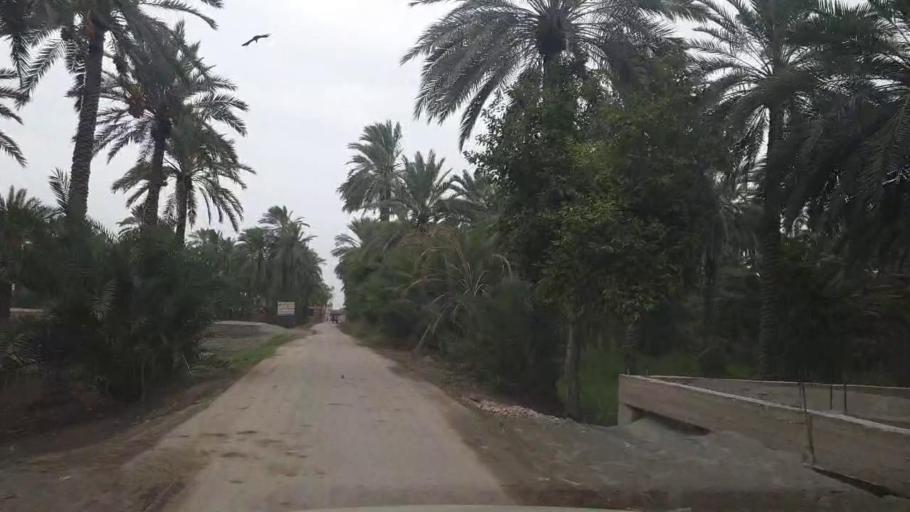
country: PK
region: Sindh
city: Khairpur
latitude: 27.5535
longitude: 68.7507
